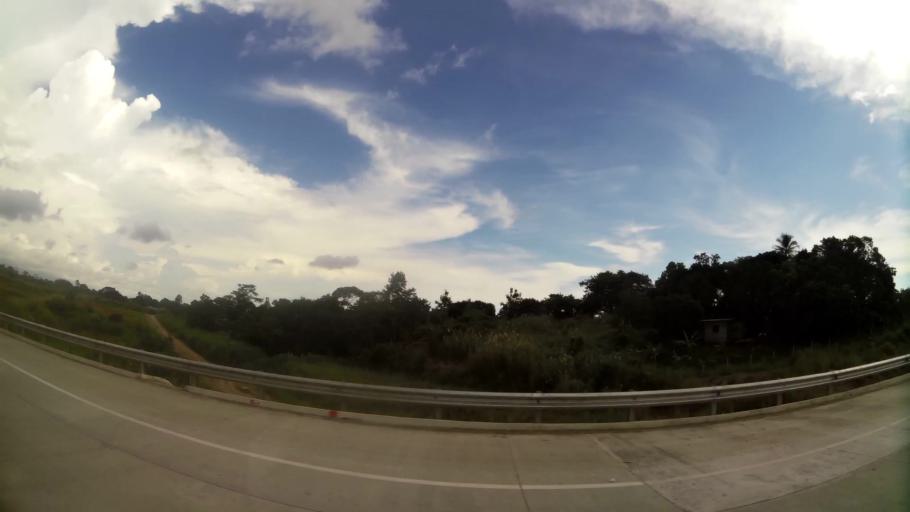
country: PA
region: Panama
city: Tocumen
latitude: 9.1010
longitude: -79.4162
